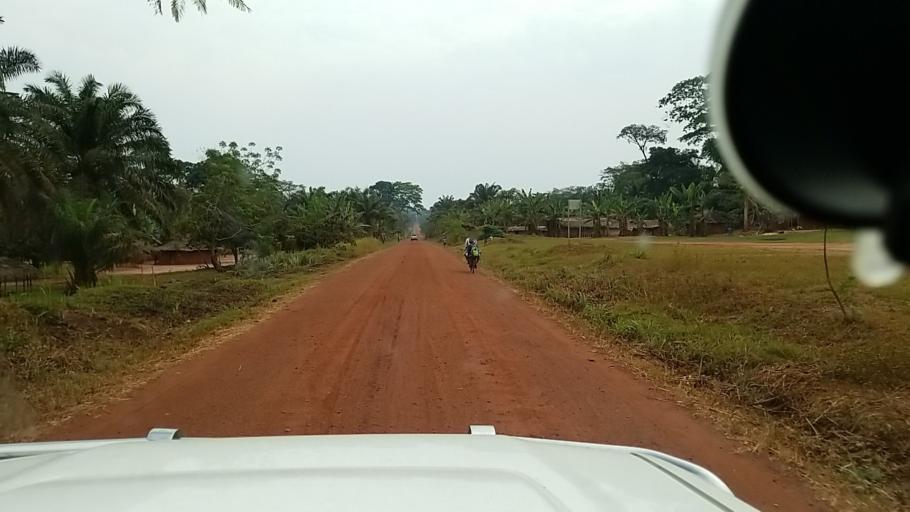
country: CD
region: Equateur
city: Gemena
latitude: 2.9636
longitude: 19.9004
